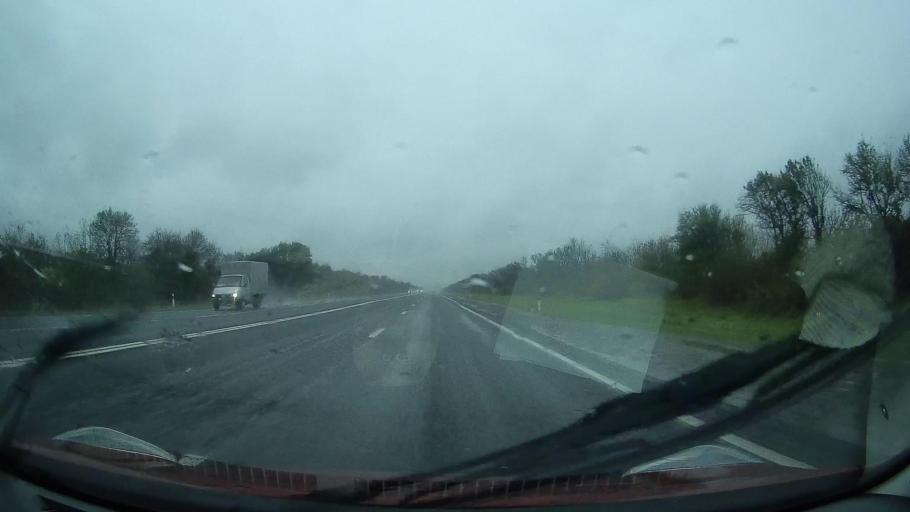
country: RU
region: Stavropol'skiy
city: Nevinnomyssk
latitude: 44.6154
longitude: 42.1078
